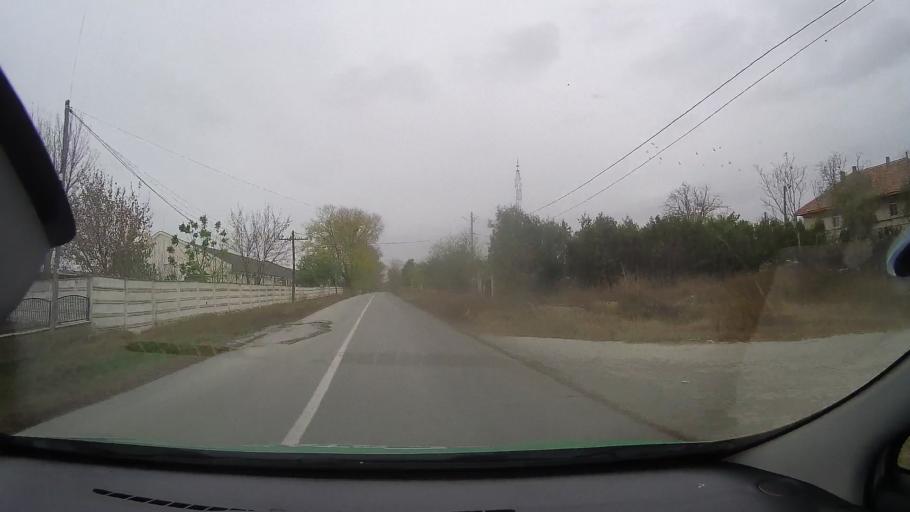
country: RO
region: Constanta
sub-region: Comuna Pantelimon
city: Pantelimon
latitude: 44.5486
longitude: 28.3299
